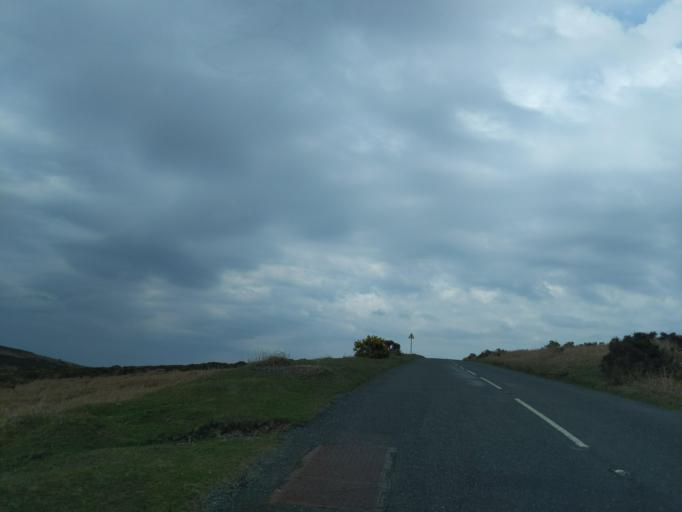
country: GB
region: England
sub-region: Devon
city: Ashburton
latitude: 50.6314
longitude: -3.8486
